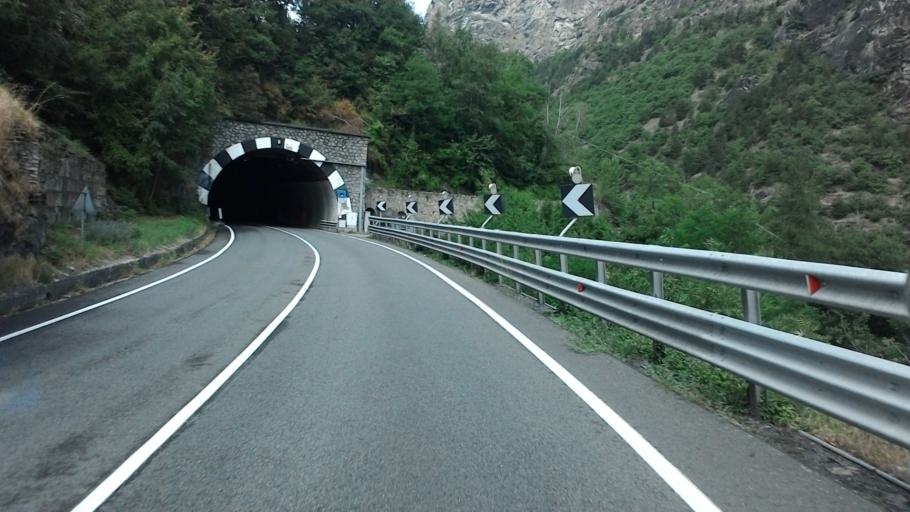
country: IT
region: Aosta Valley
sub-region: Valle d'Aosta
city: Introd
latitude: 45.7058
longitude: 7.1787
